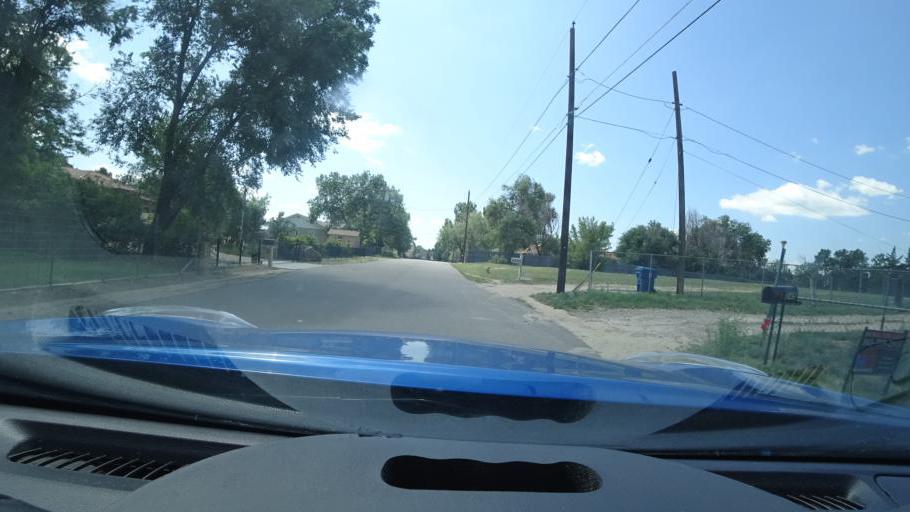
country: US
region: Colorado
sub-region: Arapahoe County
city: Glendale
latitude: 39.6943
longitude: -104.8858
